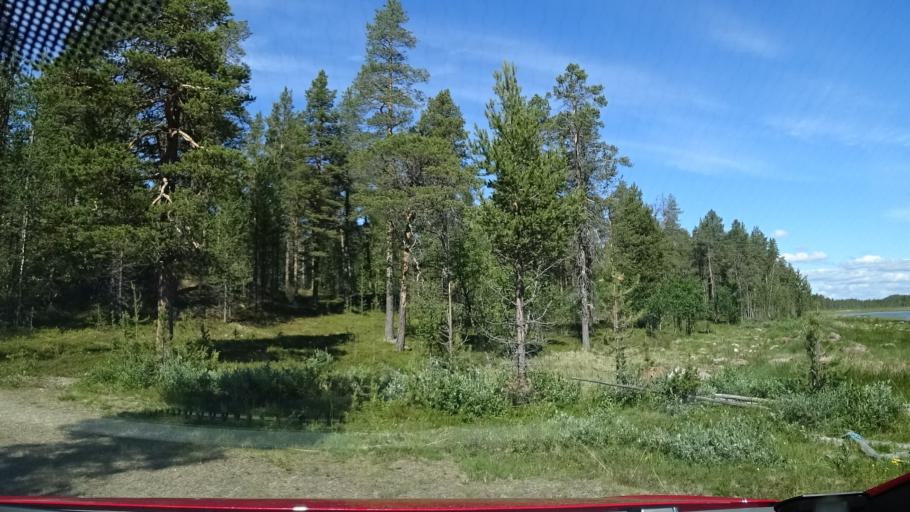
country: FI
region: Lapland
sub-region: Pohjois-Lappi
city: Inari
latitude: 68.7785
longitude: 26.5437
